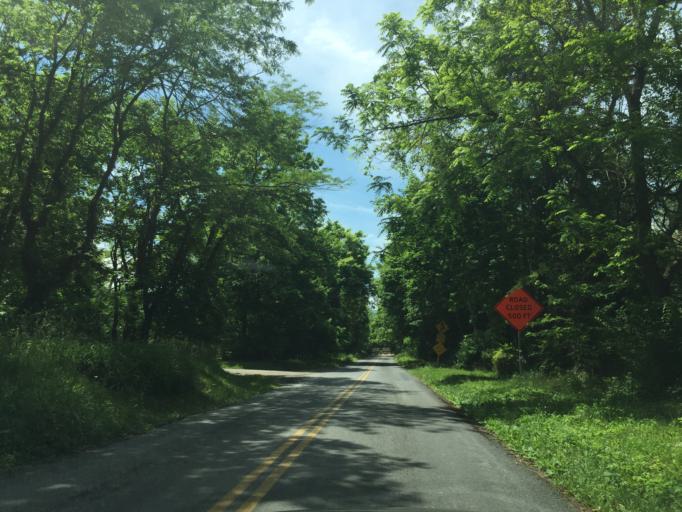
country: US
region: Virginia
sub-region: Warren County
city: Apple Mountain Lake
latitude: 38.9616
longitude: -78.1221
